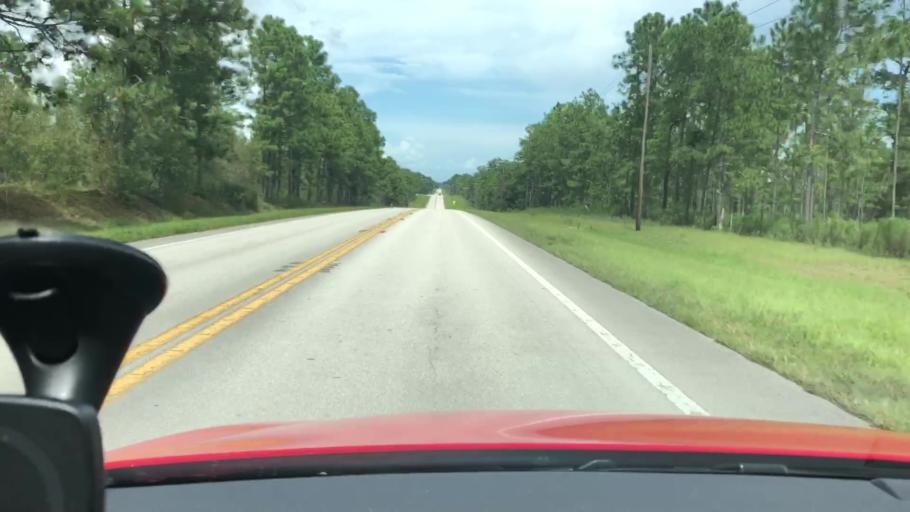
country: US
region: Florida
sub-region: Lake County
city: Mount Plymouth
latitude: 28.8548
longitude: -81.5220
